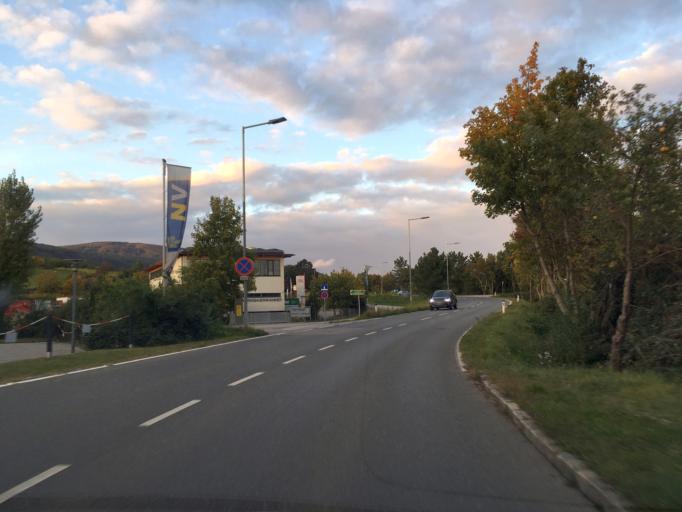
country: AT
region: Lower Austria
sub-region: Politischer Bezirk Baden
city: Pfaffstatten
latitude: 48.0132
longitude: 16.2525
